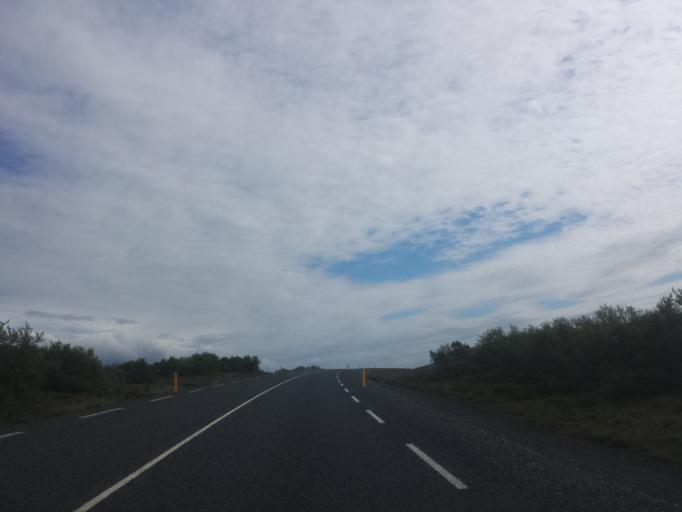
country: IS
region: Northeast
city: Husavik
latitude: 66.0029
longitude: -16.5698
